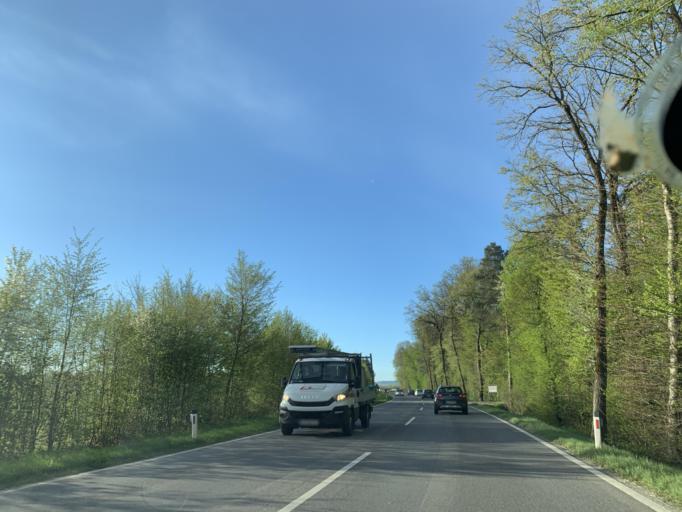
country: AT
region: Styria
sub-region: Politischer Bezirk Leibnitz
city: Lang
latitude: 46.8285
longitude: 15.5201
